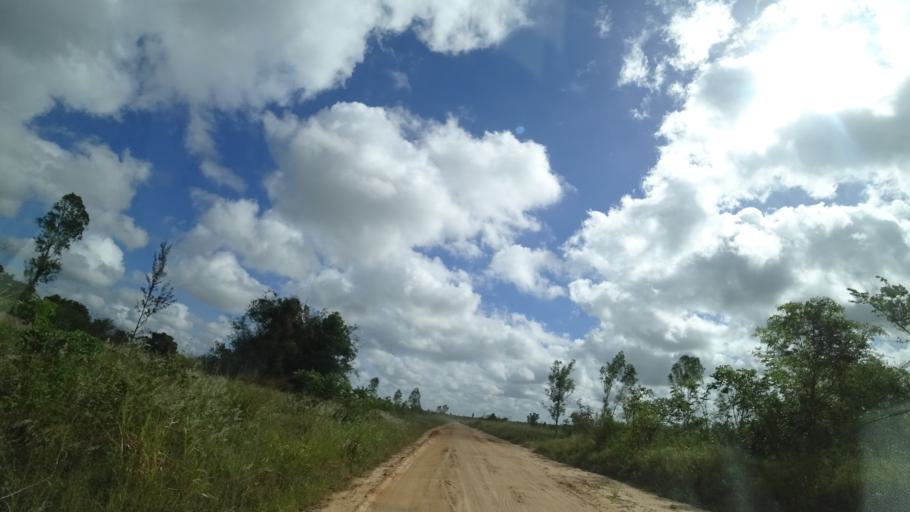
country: MZ
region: Sofala
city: Dondo
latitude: -19.4291
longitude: 34.7083
